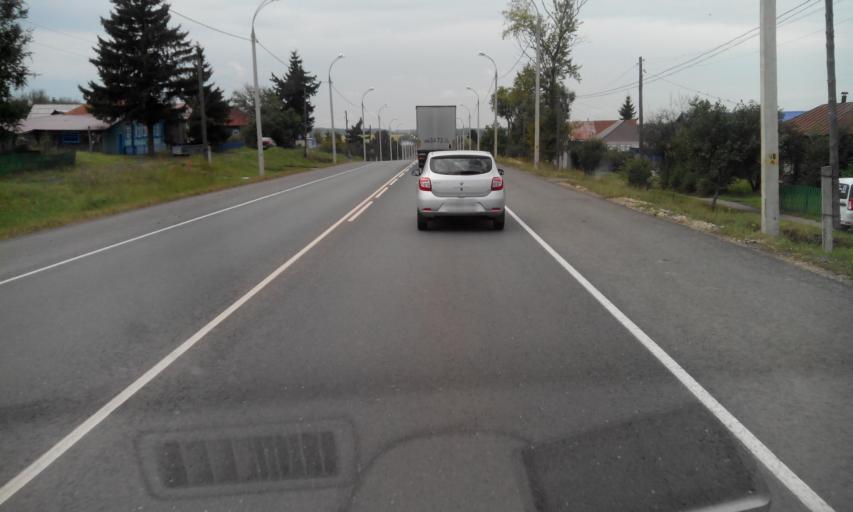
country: RU
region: Penza
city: Poselki
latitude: 53.1030
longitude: 46.4290
